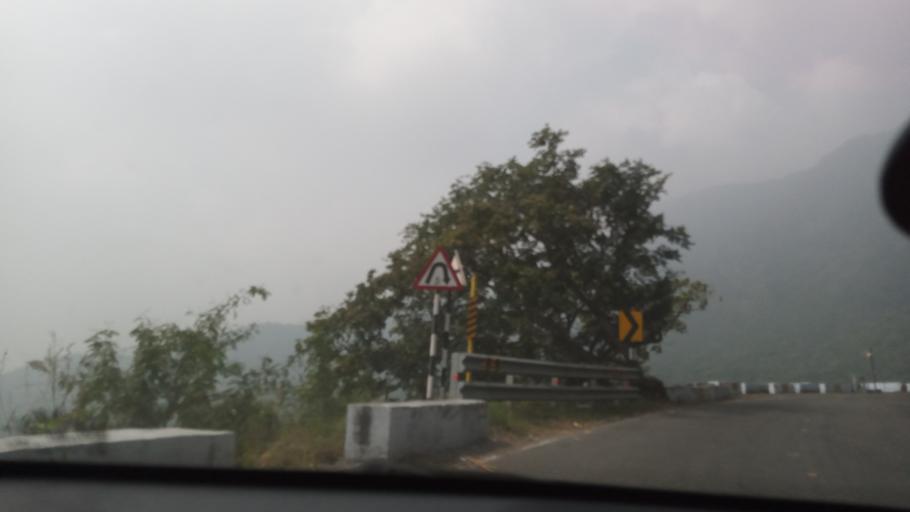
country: IN
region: Tamil Nadu
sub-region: Erode
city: Sathyamangalam
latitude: 11.5916
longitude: 77.1270
